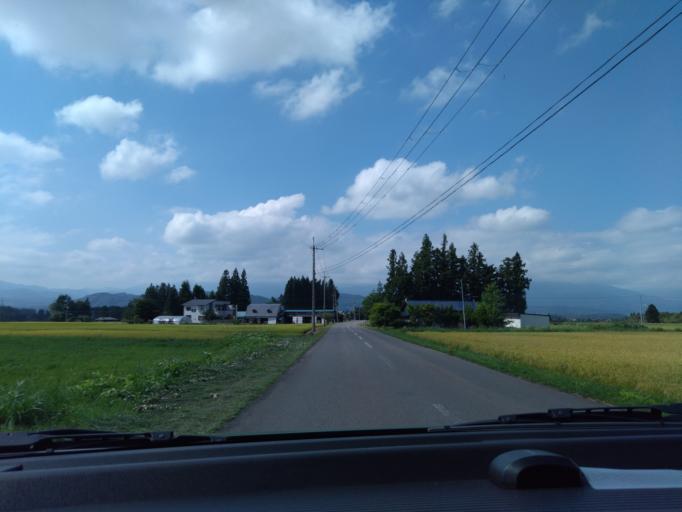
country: JP
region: Iwate
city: Shizukuishi
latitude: 39.6768
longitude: 140.9621
